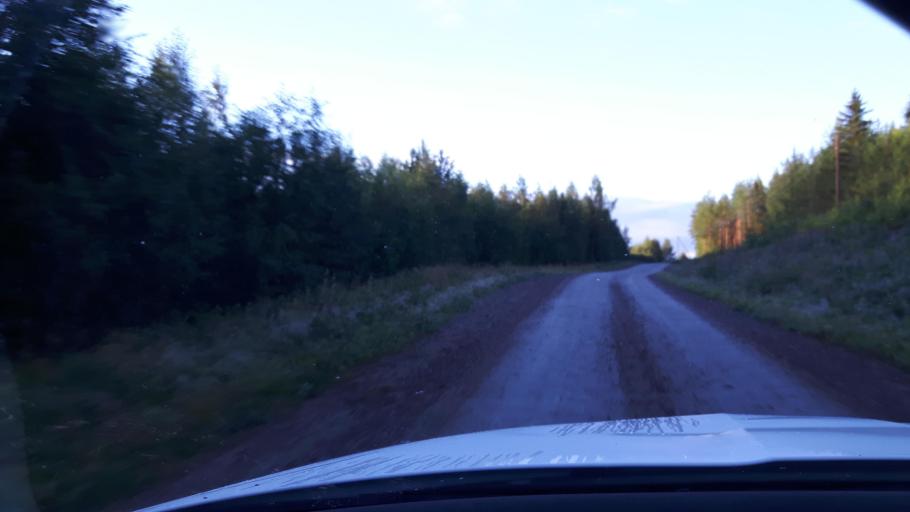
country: SE
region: Vaesternorrland
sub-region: Ange Kommun
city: Ange
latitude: 62.1575
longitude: 15.6622
